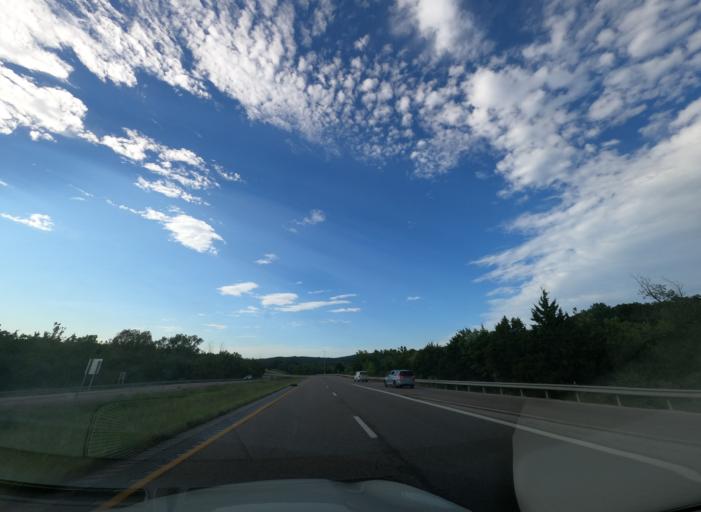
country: US
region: Missouri
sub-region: Jefferson County
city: Crystal City
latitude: 38.1599
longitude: -90.3587
